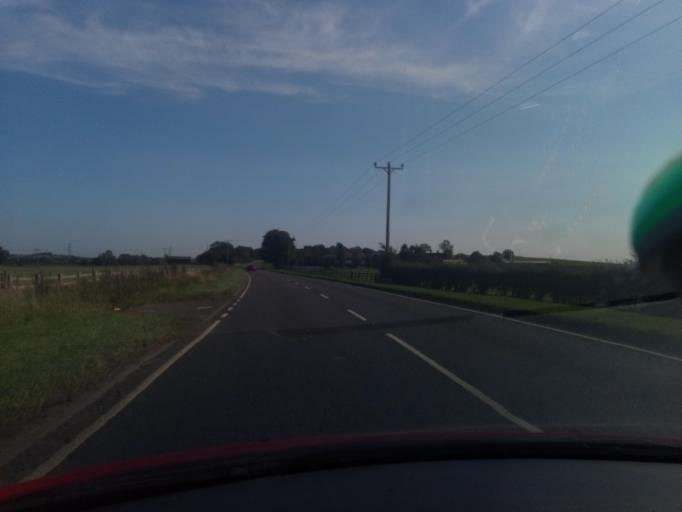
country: GB
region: England
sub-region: North Yorkshire
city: Angram Grange
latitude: 54.1898
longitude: -1.2741
